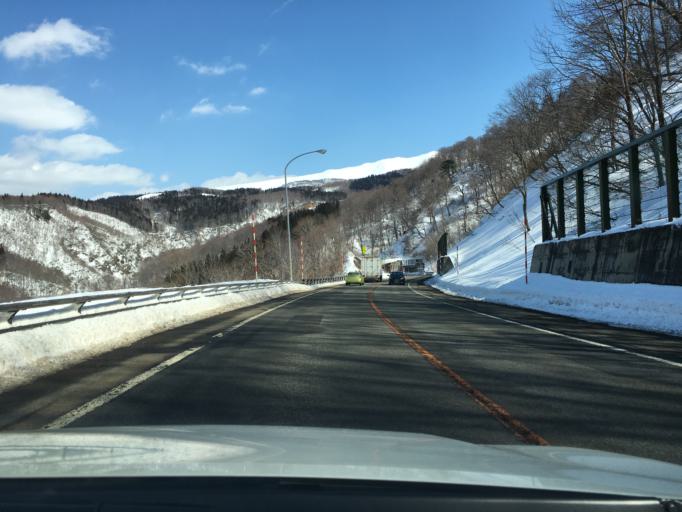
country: JP
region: Yamagata
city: Tsuruoka
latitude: 38.5622
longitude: 139.9349
